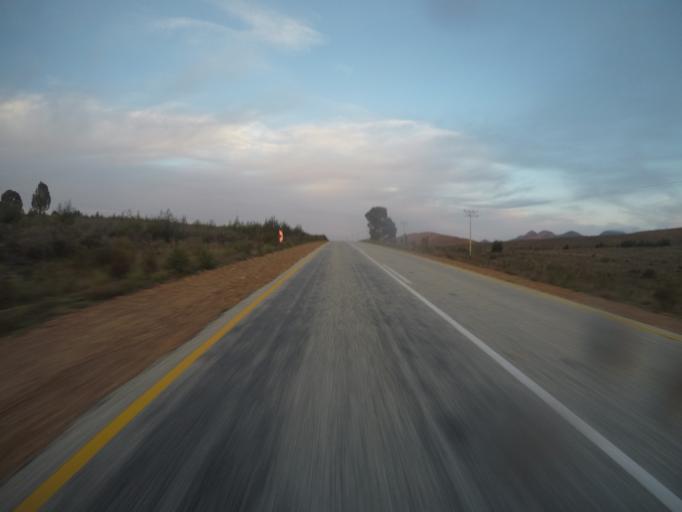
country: ZA
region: Western Cape
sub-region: Eden District Municipality
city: Plettenberg Bay
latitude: -33.7373
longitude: 23.4168
